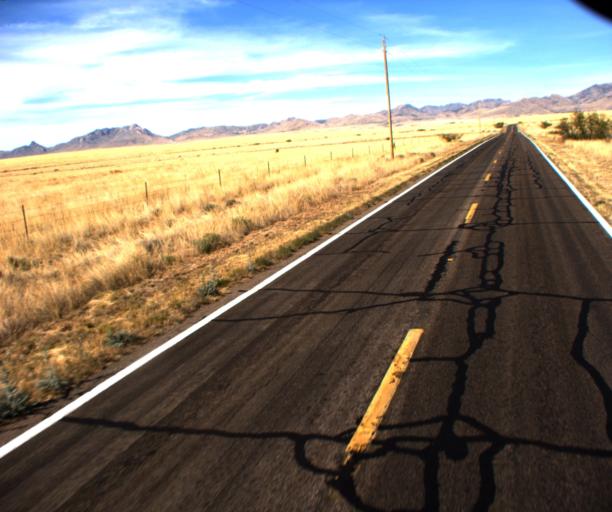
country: US
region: Arizona
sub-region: Cochise County
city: Willcox
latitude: 31.9879
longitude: -109.4534
